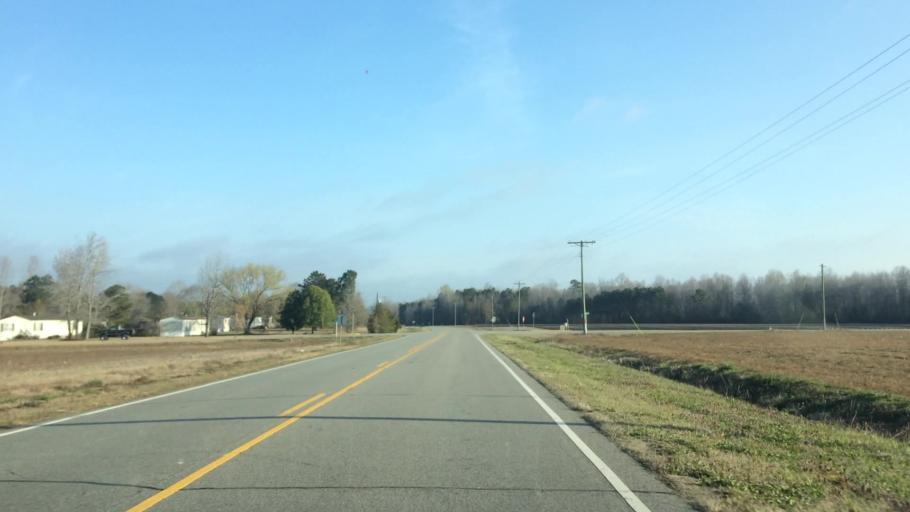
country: US
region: North Carolina
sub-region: Edgecombe County
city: Pinetops
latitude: 35.7110
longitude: -77.6331
